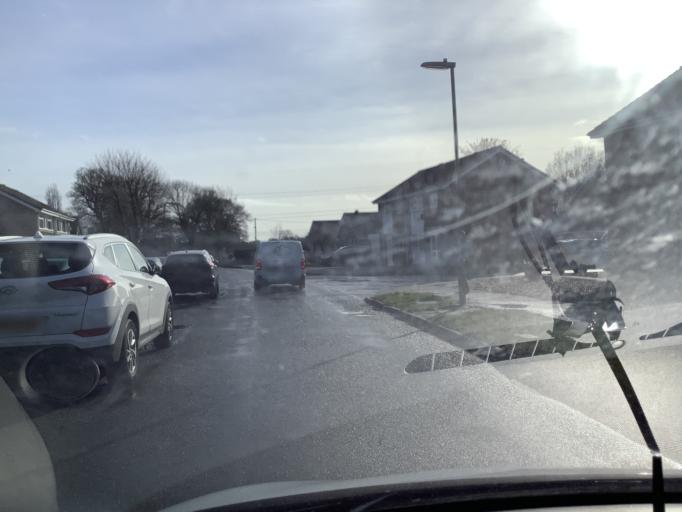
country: GB
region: England
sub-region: Hampshire
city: Hythe
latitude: 50.8269
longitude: -1.3920
